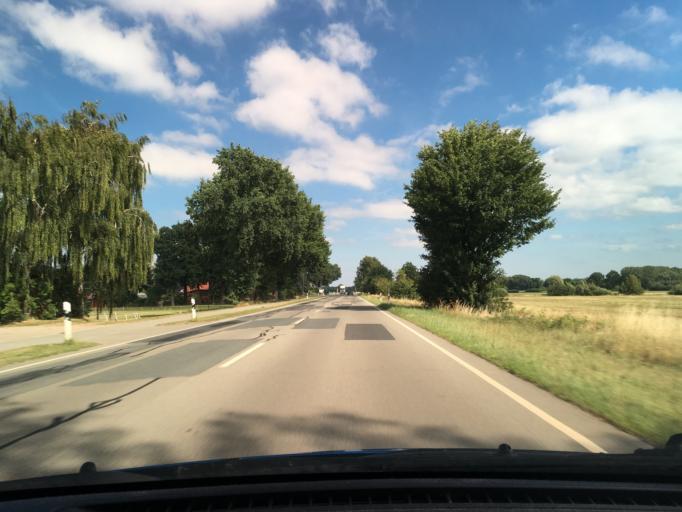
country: DE
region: Lower Saxony
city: Stelle
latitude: 53.3683
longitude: 10.1578
